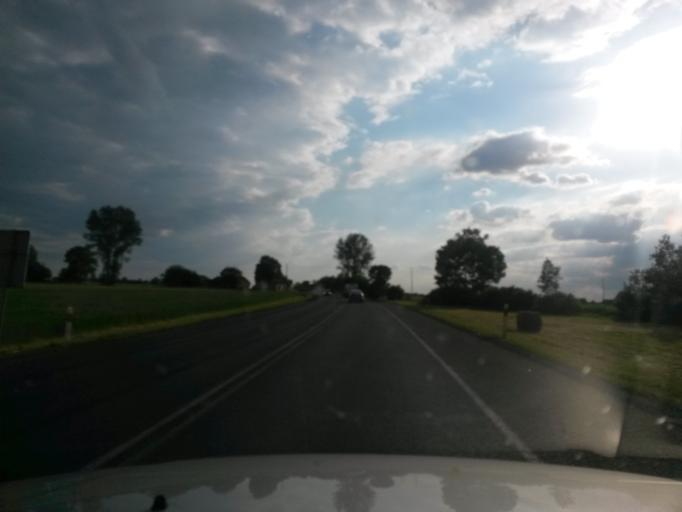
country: PL
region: Lodz Voivodeship
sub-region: Powiat piotrkowski
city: Grabica
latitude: 51.4218
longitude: 19.4919
